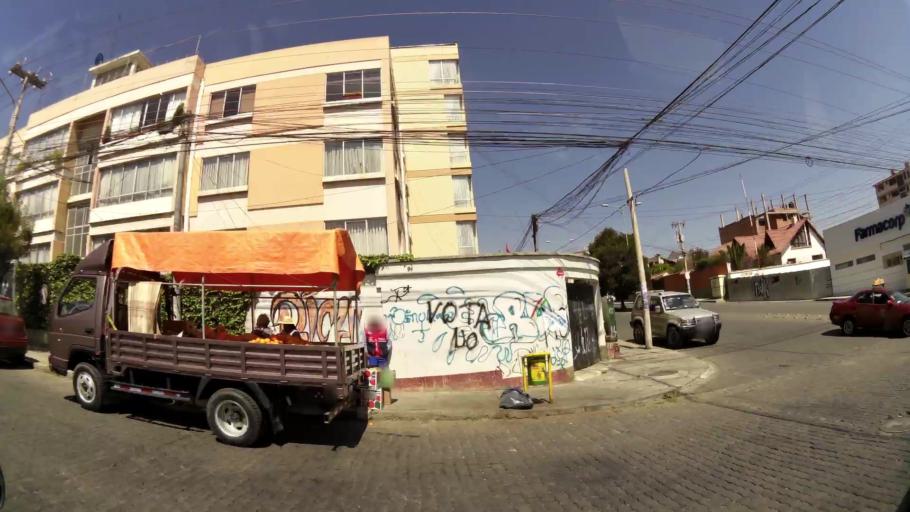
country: BO
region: La Paz
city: La Paz
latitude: -16.5407
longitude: -68.0670
